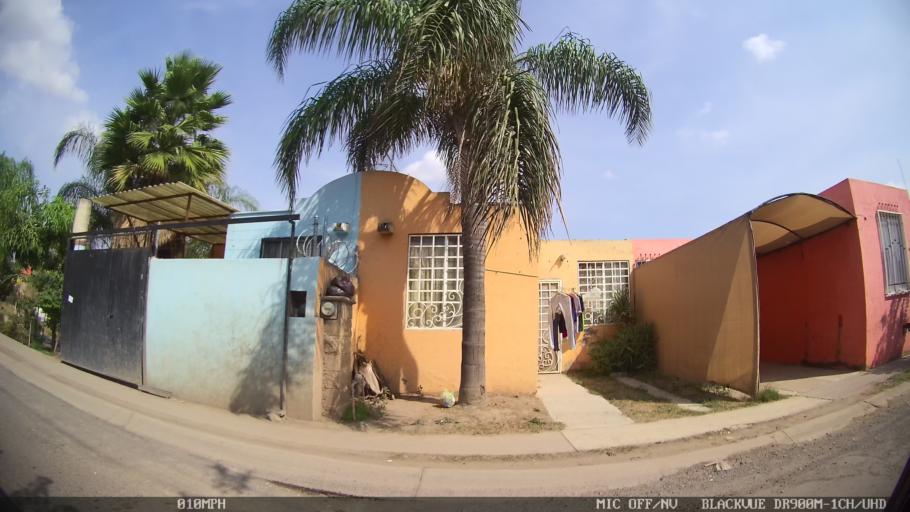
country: MX
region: Jalisco
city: Coyula
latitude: 20.6516
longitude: -103.2140
